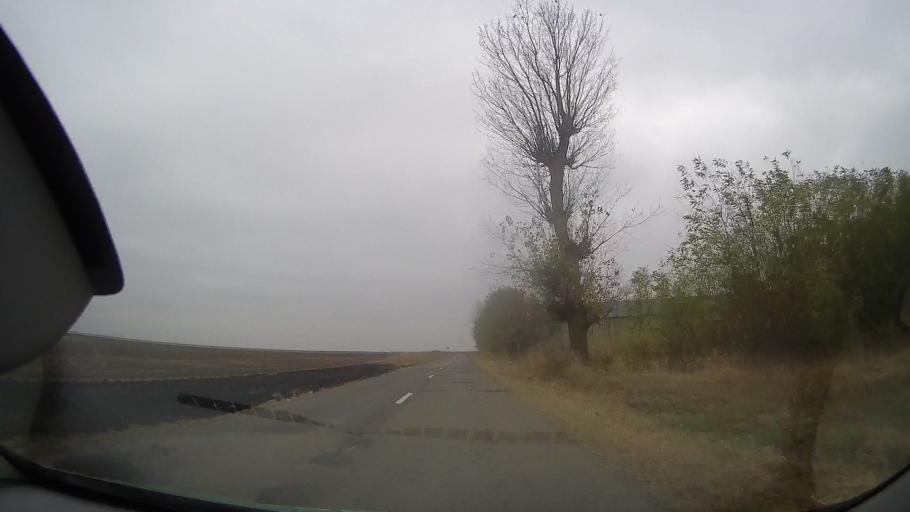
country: RO
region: Ialomita
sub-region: Comuna Valea Macrisului
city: Valea Macrisului
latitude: 44.7396
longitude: 26.8631
